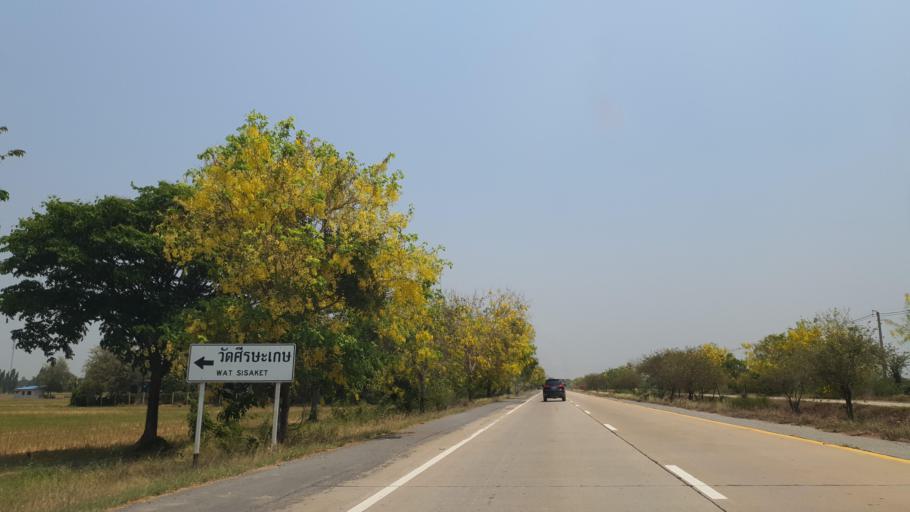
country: TH
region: Suphan Buri
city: Suphan Buri
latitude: 14.5140
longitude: 100.0526
